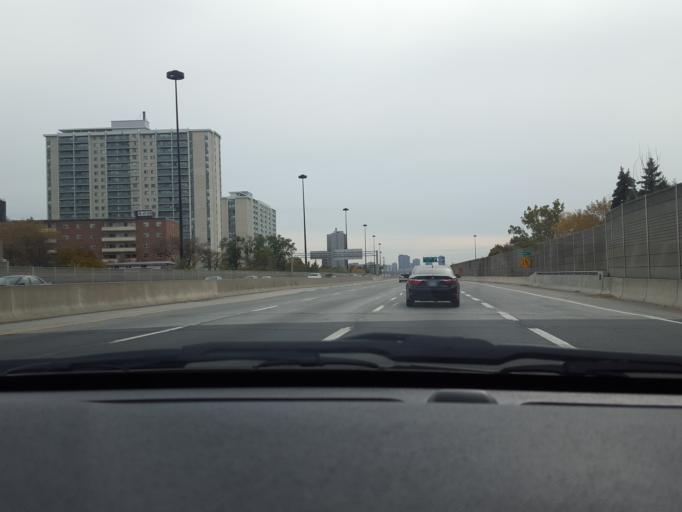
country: CA
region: Ontario
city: Willowdale
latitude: 43.7626
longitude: -79.3370
